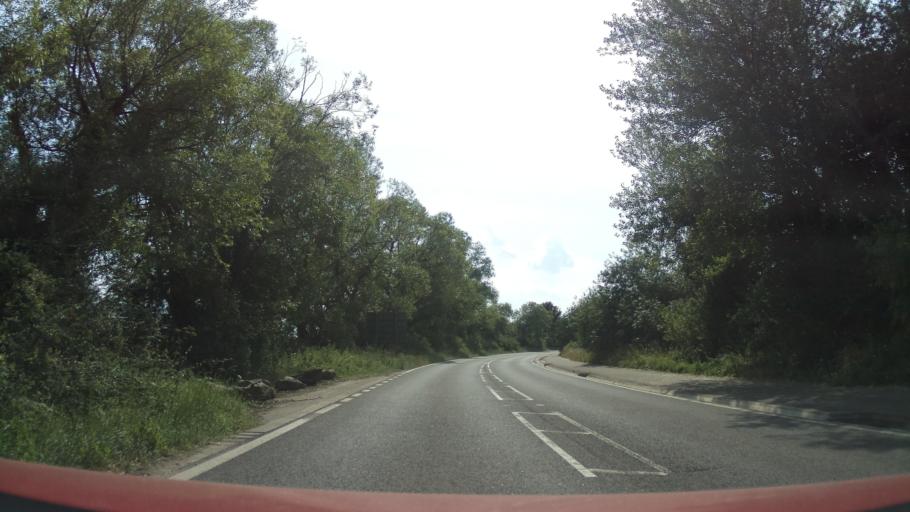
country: GB
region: England
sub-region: Wiltshire
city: Leigh
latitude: 51.6566
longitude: -1.9184
